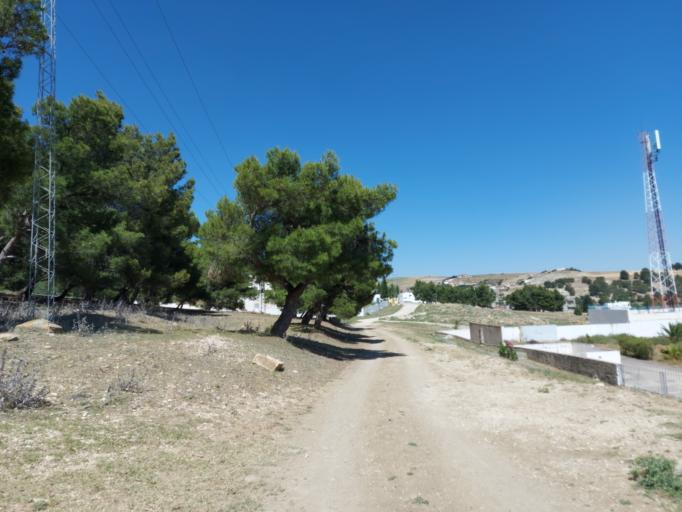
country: TN
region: Kef
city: El Kef
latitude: 36.1829
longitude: 8.7255
